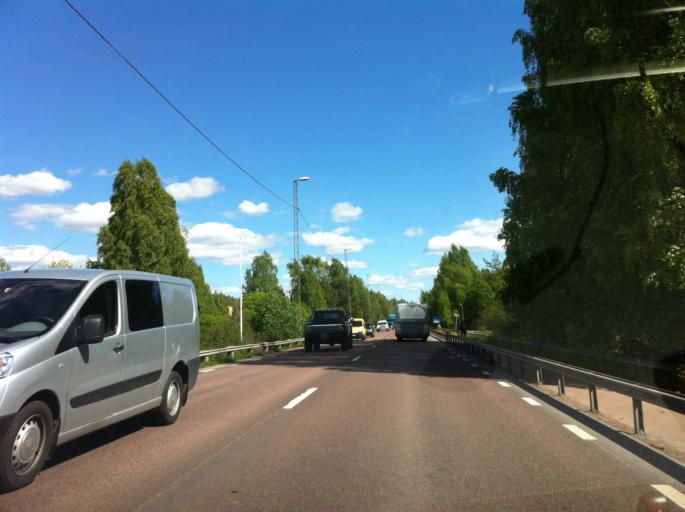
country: SE
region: Dalarna
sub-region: Mora Kommun
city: Mora
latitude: 61.0096
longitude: 14.5797
